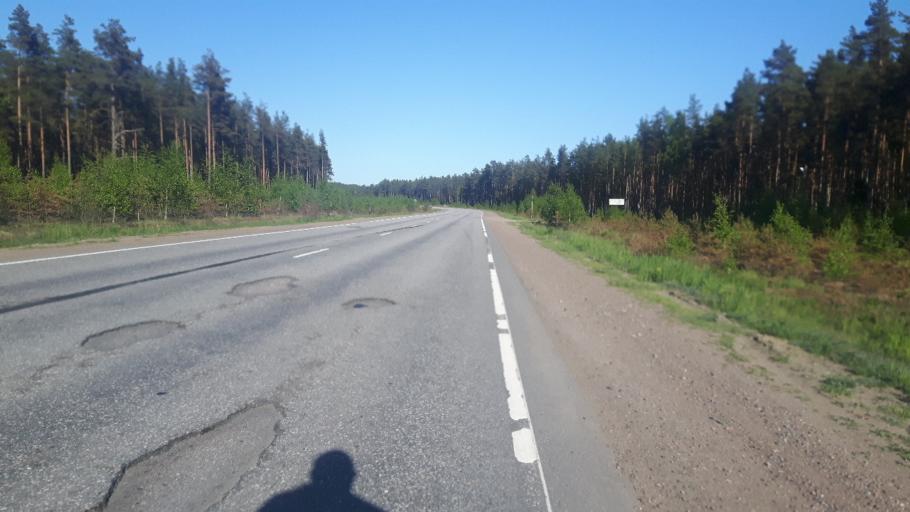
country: RU
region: Leningrad
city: Lebyazh'ye
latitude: 60.1676
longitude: 29.2450
